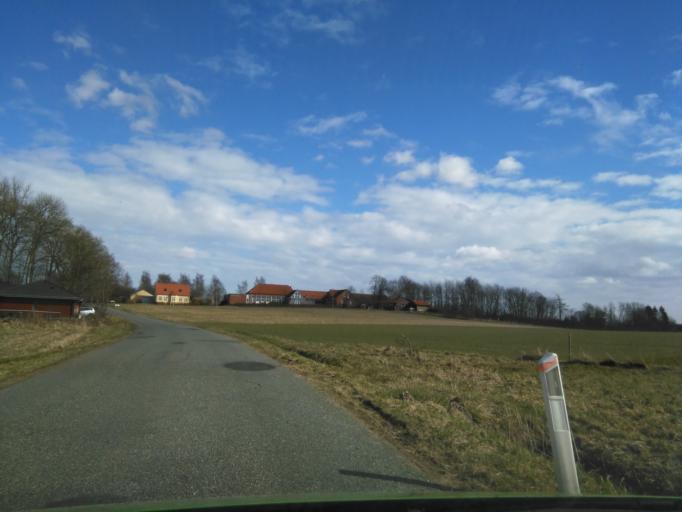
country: DK
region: Central Jutland
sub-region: Skanderborg Kommune
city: Skanderborg
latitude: 55.9201
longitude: 9.9936
